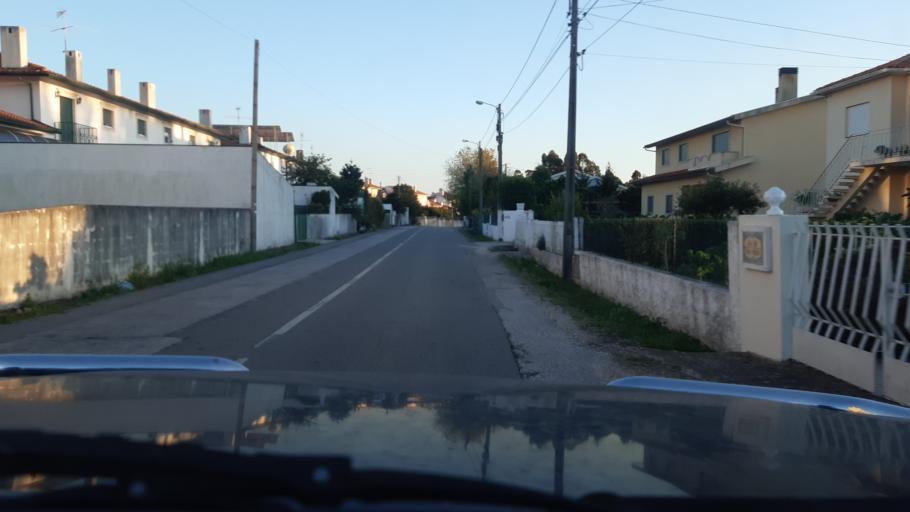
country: PT
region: Aveiro
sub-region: Agueda
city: Agueda
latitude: 40.5809
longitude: -8.4637
